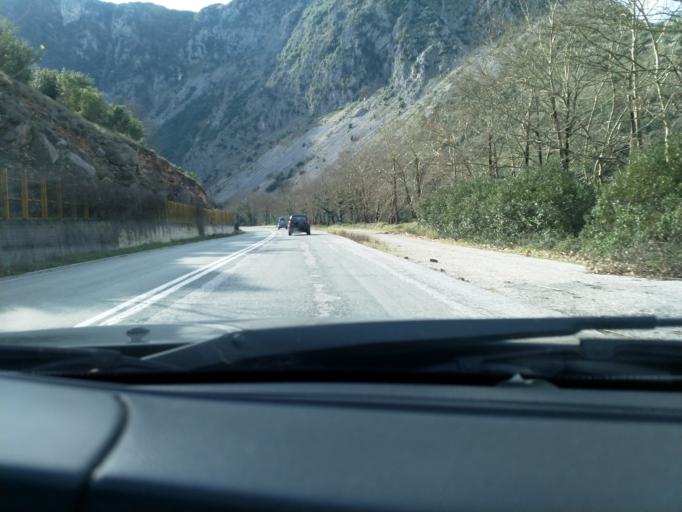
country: GR
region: Epirus
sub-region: Nomos Prevezis
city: Pappadates
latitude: 39.4037
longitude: 20.8349
